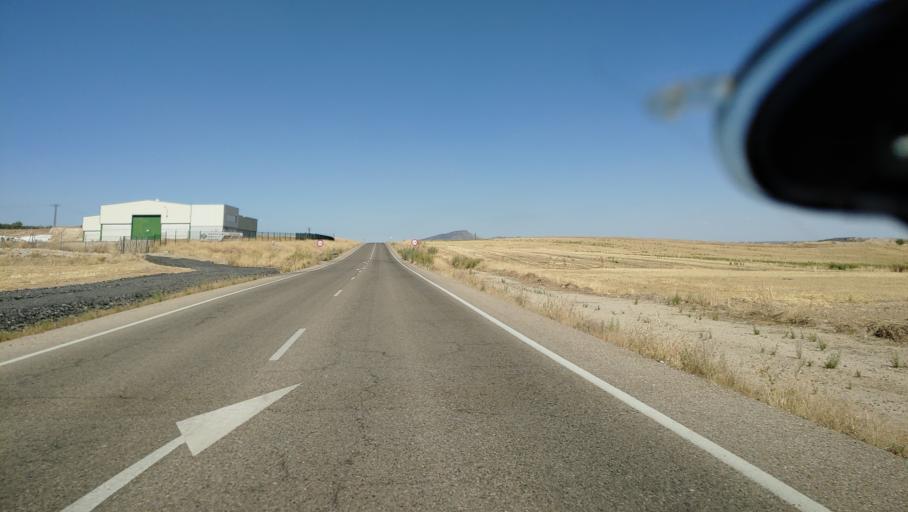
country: ES
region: Castille-La Mancha
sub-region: Province of Toledo
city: Pulgar
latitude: 39.6794
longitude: -4.1780
